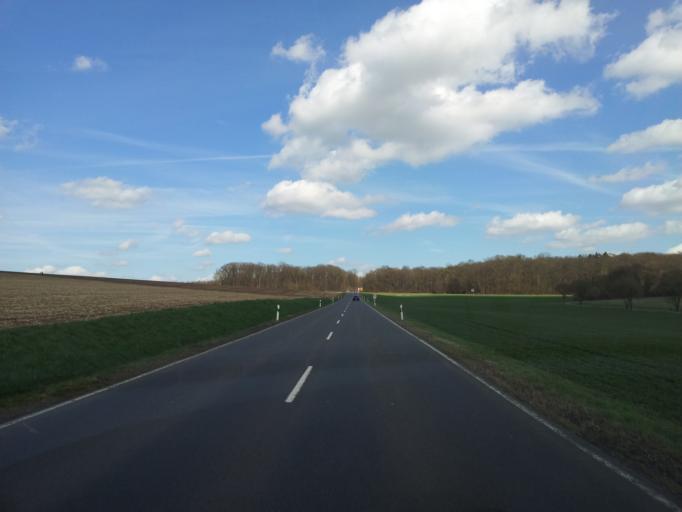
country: DE
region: Bavaria
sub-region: Regierungsbezirk Unterfranken
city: Waldbrunn
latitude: 49.7148
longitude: 9.7950
